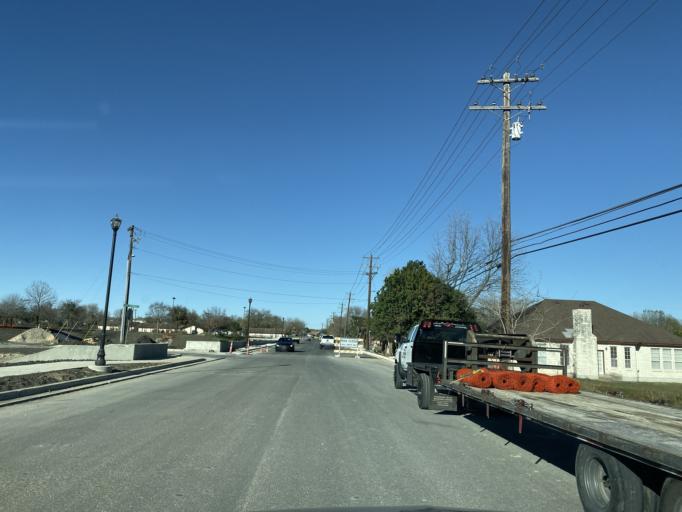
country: US
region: Texas
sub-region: Hays County
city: Kyle
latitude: 29.9943
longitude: -97.8761
